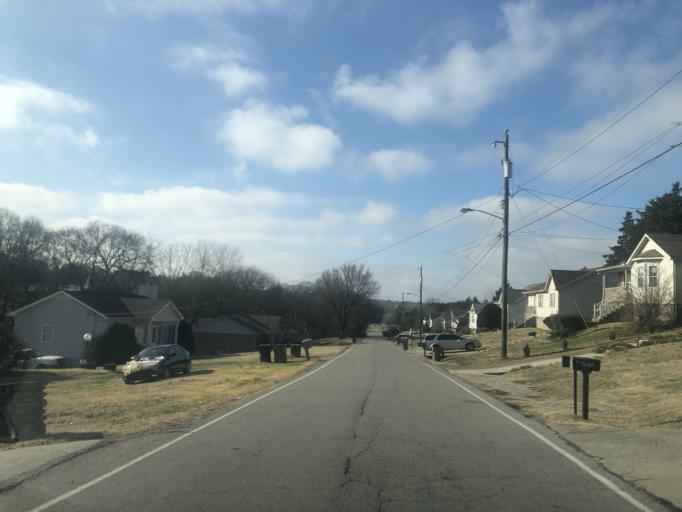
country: US
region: Tennessee
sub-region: Rutherford County
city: La Vergne
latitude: 36.0589
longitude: -86.6645
